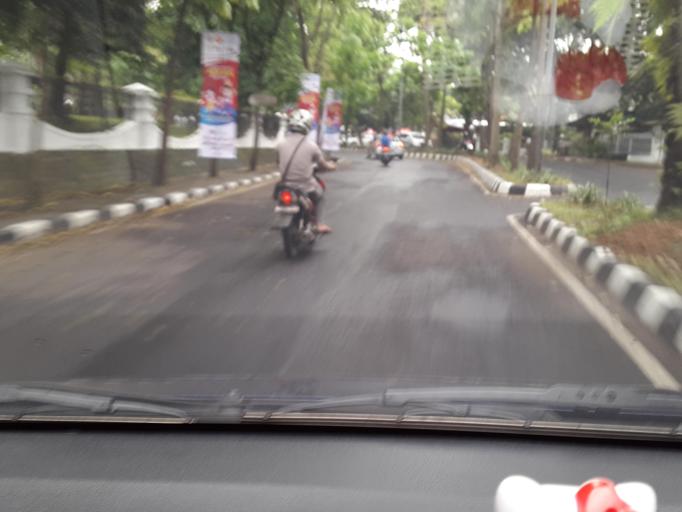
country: ID
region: West Java
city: Bandung
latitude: -6.9037
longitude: 107.6191
